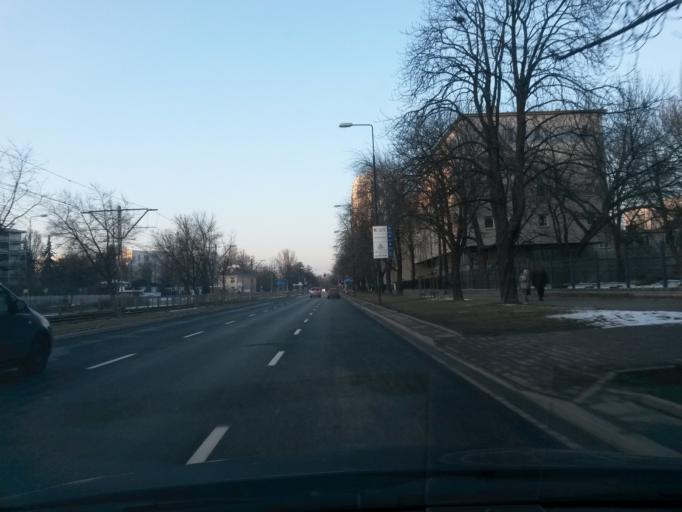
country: PL
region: Masovian Voivodeship
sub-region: Warszawa
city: Ochota
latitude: 52.2043
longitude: 20.9999
